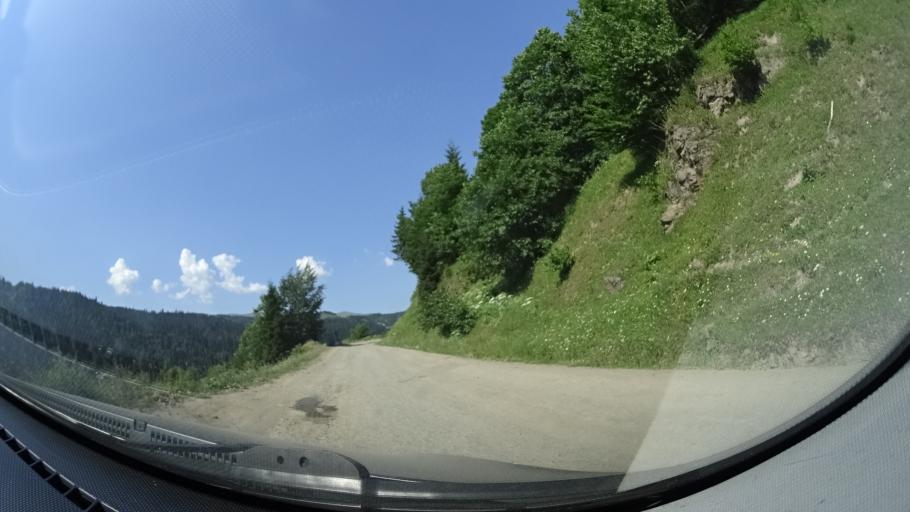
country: GE
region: Ajaria
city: Dioknisi
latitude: 41.6511
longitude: 42.4605
